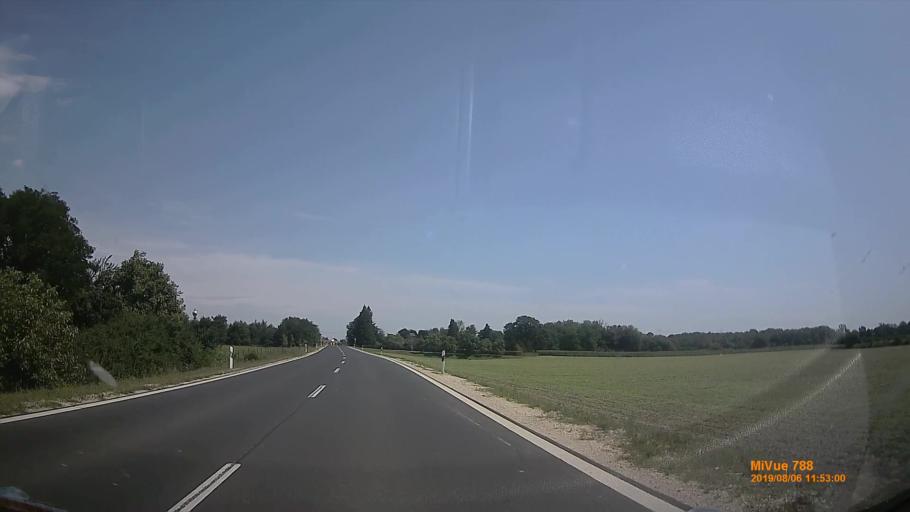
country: HU
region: Vas
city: Kormend
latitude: 47.0389
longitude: 16.6617
